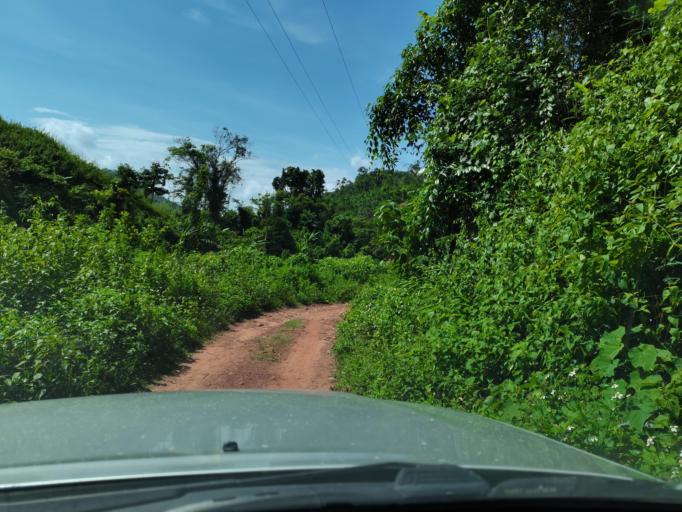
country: LA
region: Loungnamtha
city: Muang Nale
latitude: 20.5316
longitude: 101.0647
